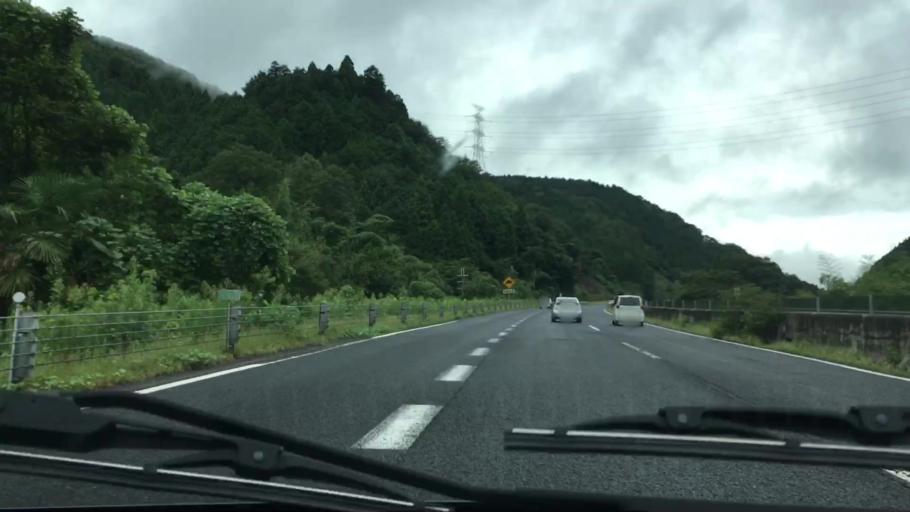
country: JP
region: Hyogo
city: Yamazakicho-nakabirose
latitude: 35.0366
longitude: 134.4760
